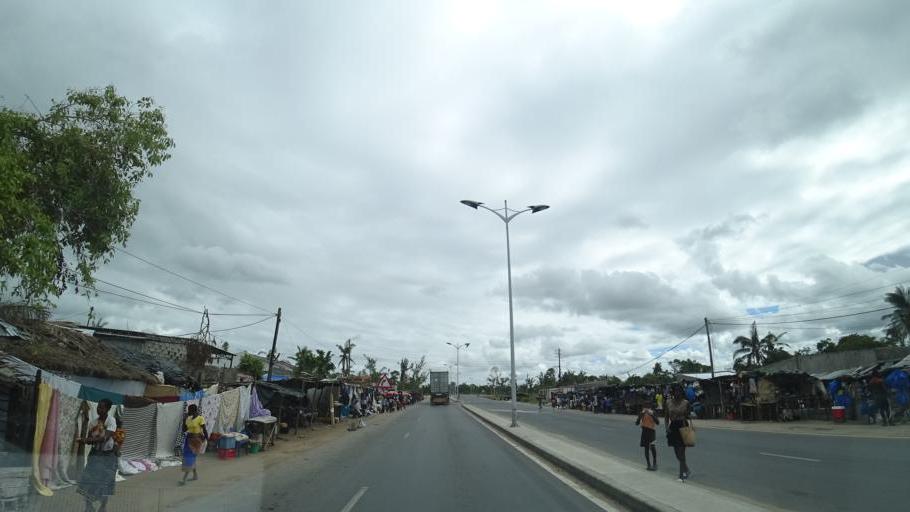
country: MZ
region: Sofala
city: Dondo
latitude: -19.6930
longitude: 34.7790
